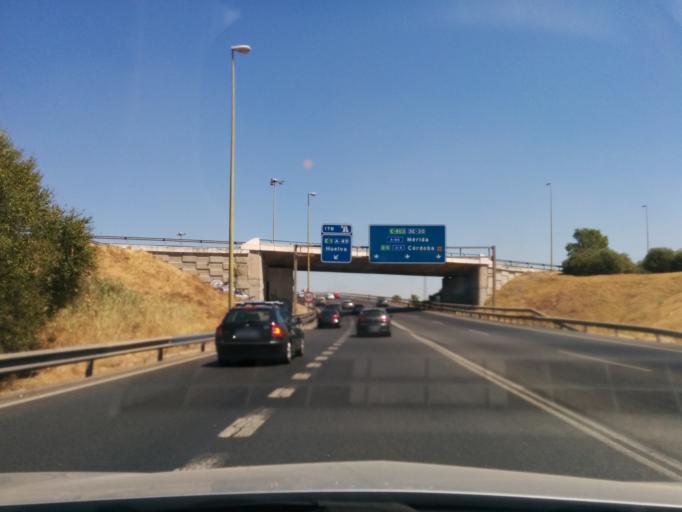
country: ES
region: Andalusia
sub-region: Provincia de Sevilla
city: Camas
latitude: 37.3873
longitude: -6.0251
